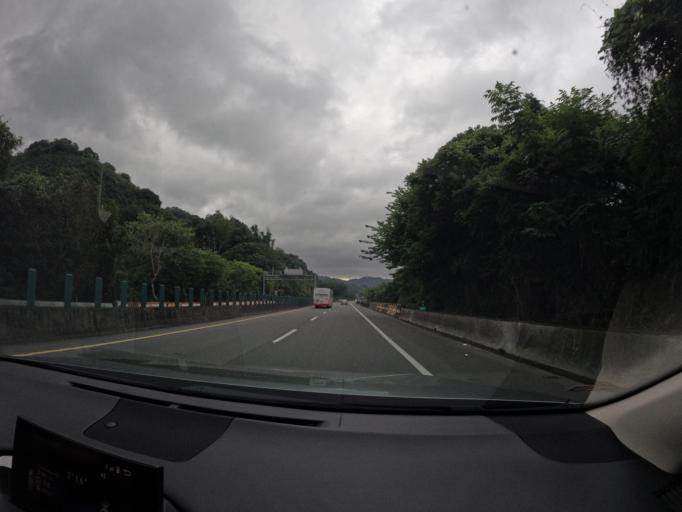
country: TW
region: Taiwan
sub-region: Miaoli
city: Miaoli
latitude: 24.4640
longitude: 120.8348
